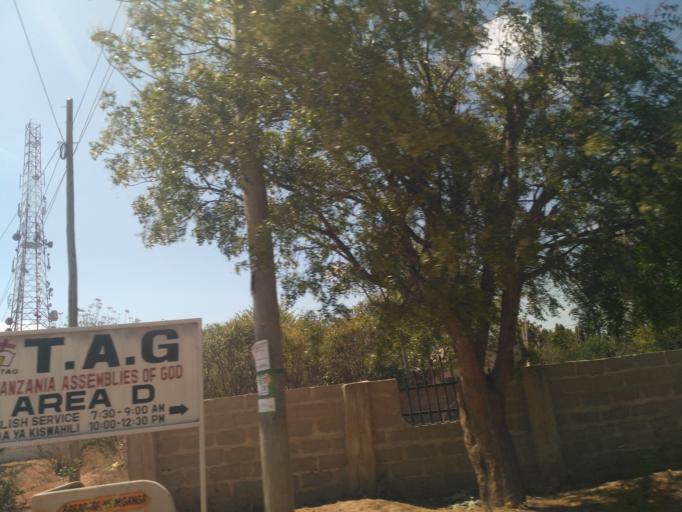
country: TZ
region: Dodoma
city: Dodoma
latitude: -6.1613
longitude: 35.7621
